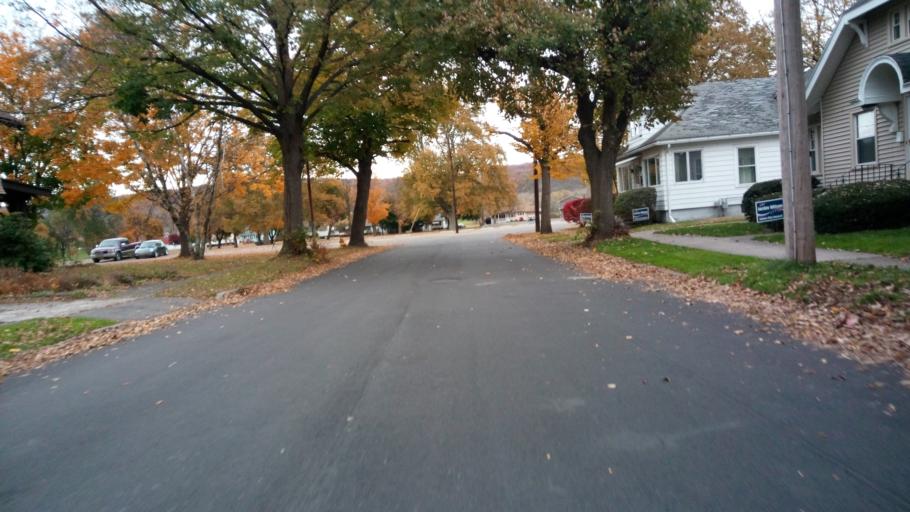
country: US
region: New York
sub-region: Chemung County
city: Elmira
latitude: 42.0838
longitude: -76.7930
